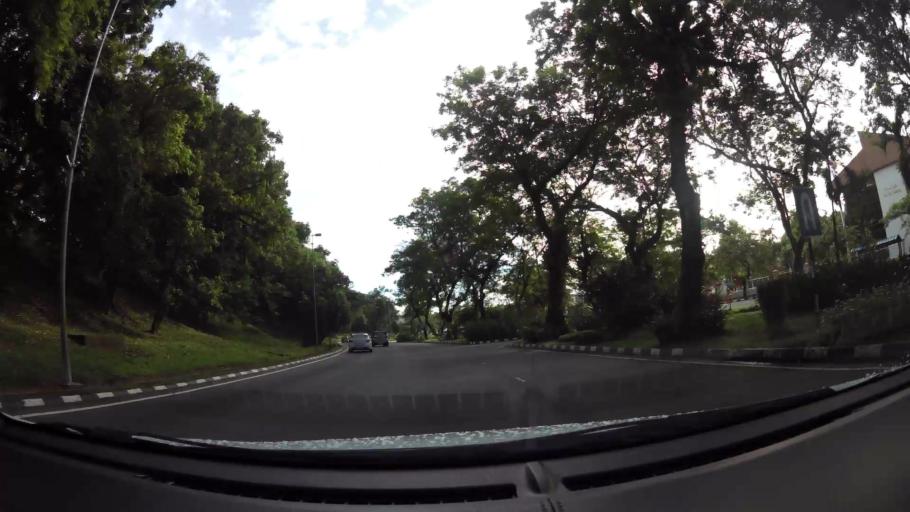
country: BN
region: Brunei and Muara
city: Bandar Seri Begawan
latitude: 4.8910
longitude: 114.9331
